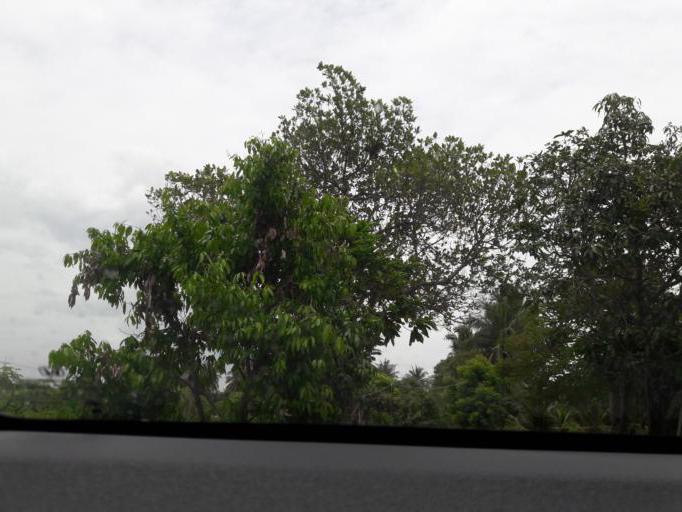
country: TH
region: Ratchaburi
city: Damnoen Saduak
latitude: 13.5736
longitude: 99.9930
